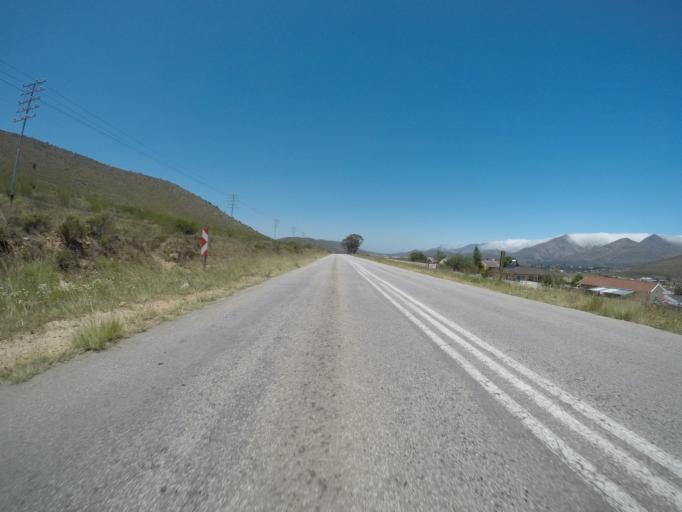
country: ZA
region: Eastern Cape
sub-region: Cacadu District Municipality
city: Kareedouw
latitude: -33.8276
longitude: 23.8797
